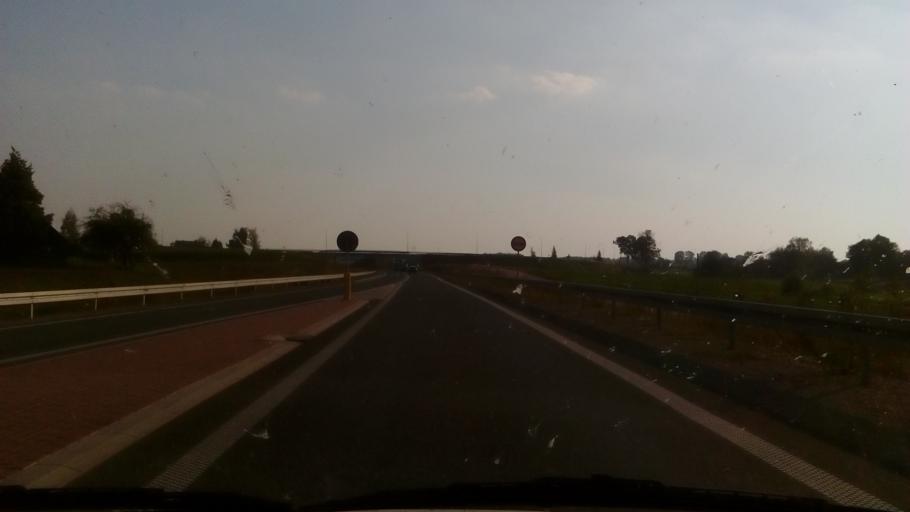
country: PL
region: Podlasie
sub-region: Powiat grajewski
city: Rajgrod
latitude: 53.7770
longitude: 22.8366
